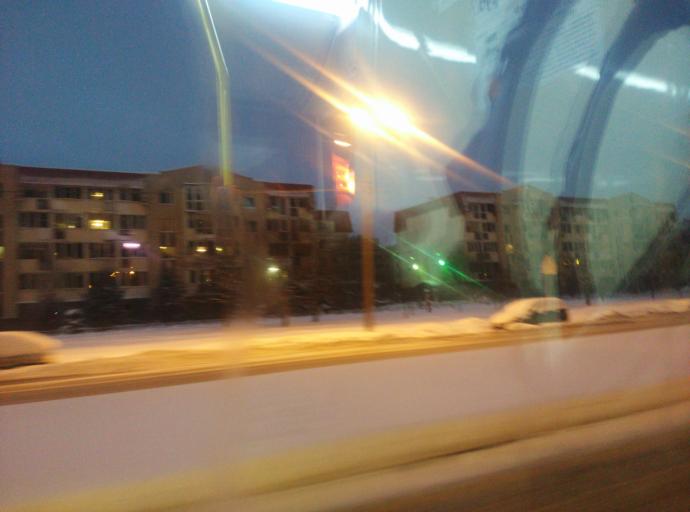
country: RU
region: St.-Petersburg
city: Kolomyagi
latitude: 60.0180
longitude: 30.2732
